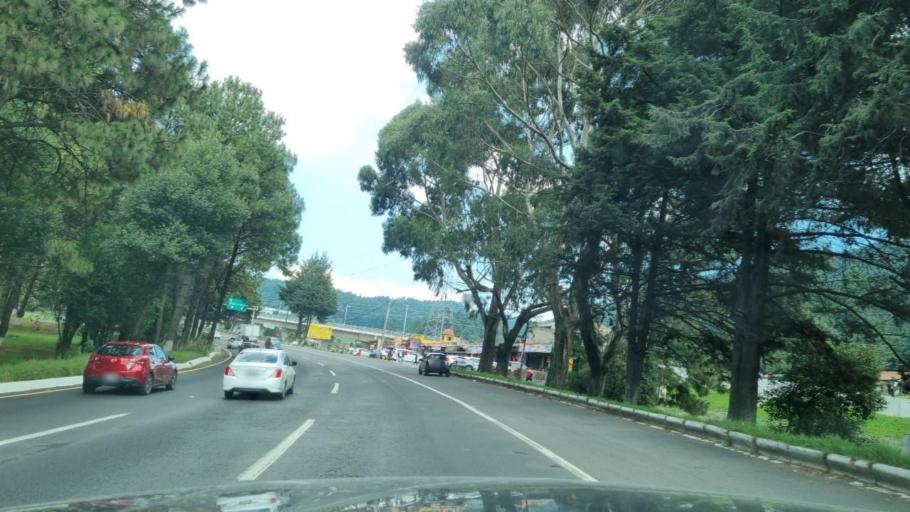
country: MX
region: Morelos
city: San Jeronimo Acazulco
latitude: 19.2961
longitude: -99.4006
